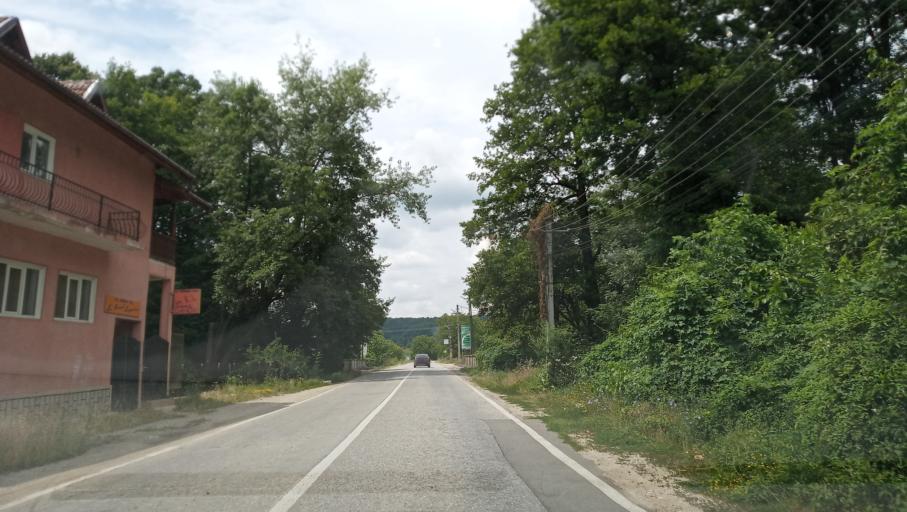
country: RO
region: Gorj
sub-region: Comuna Arcani
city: Arcani
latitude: 45.0887
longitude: 23.1340
